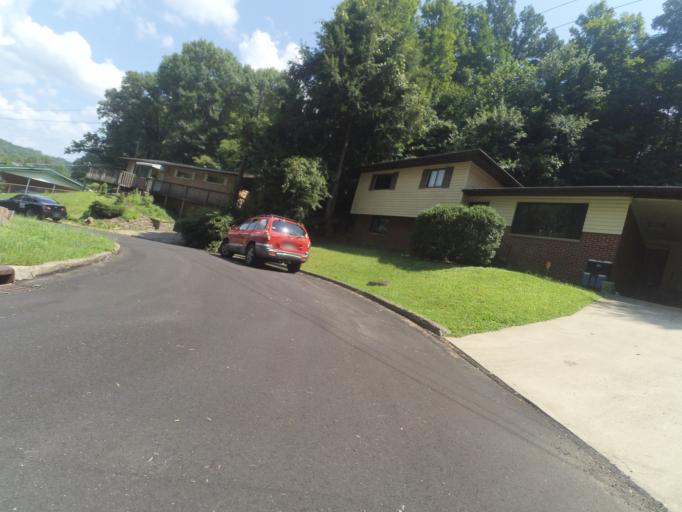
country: US
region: West Virginia
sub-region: Cabell County
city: Huntington
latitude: 38.3972
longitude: -82.4304
